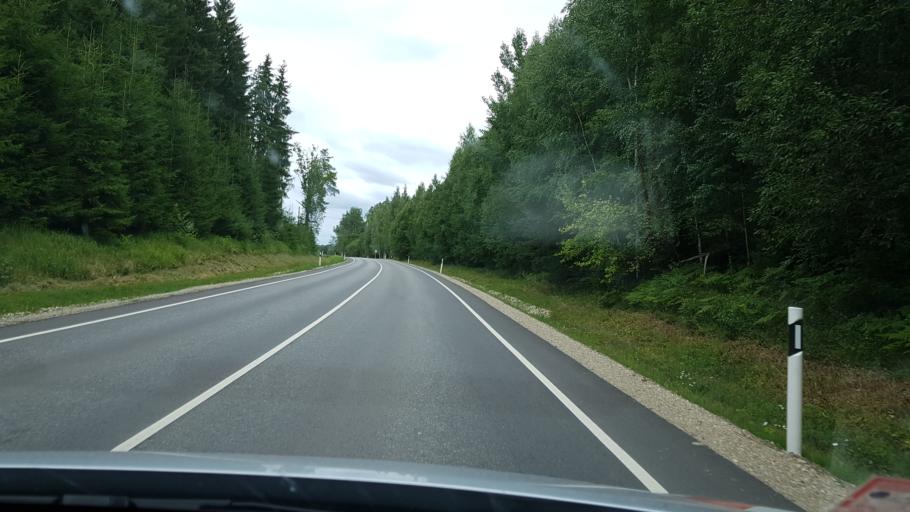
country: EE
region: Polvamaa
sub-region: Polva linn
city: Polva
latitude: 58.0223
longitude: 27.1635
